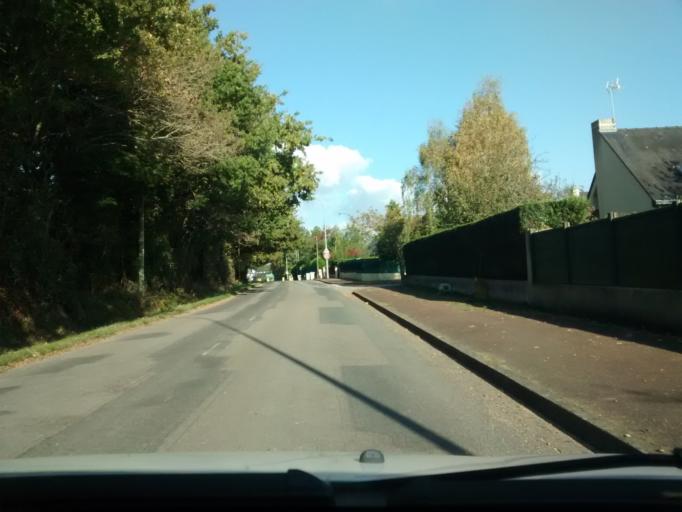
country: FR
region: Pays de la Loire
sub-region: Departement de la Loire-Atlantique
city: Sautron
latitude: 47.2613
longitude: -1.6824
